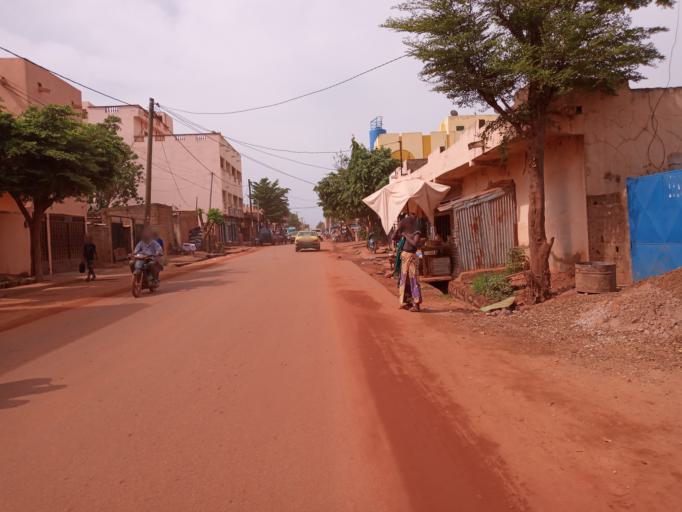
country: ML
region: Bamako
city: Bamako
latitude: 12.5570
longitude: -7.9903
